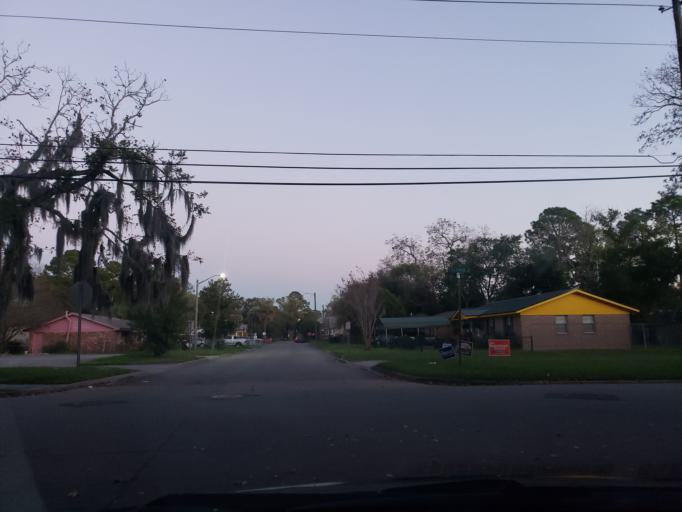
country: US
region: Georgia
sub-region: Chatham County
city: Savannah
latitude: 32.0579
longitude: -81.0846
